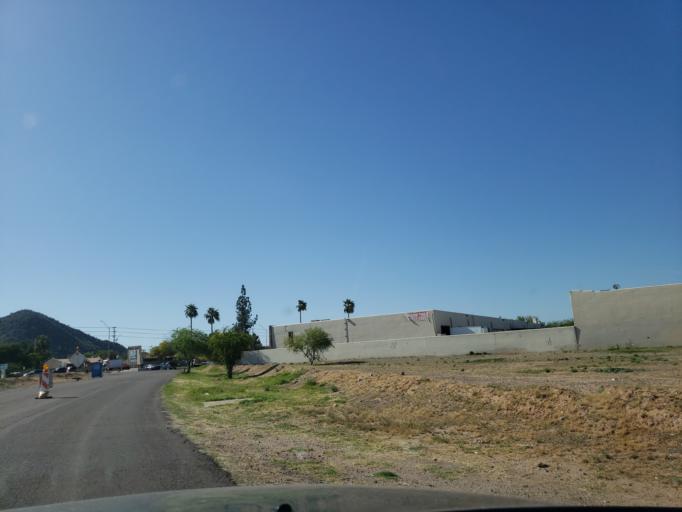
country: US
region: Arizona
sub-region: Maricopa County
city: Paradise Valley
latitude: 33.6735
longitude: -112.0297
